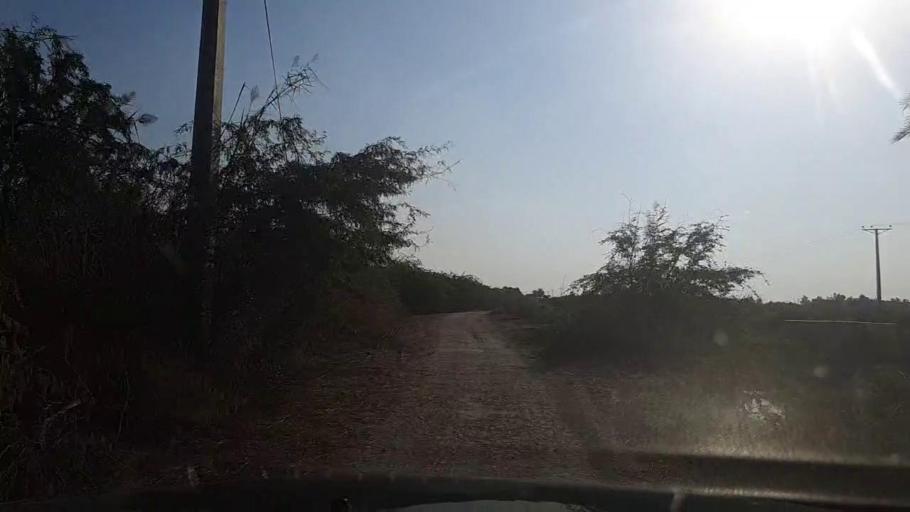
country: PK
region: Sindh
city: Gharo
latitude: 24.7105
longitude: 67.6837
